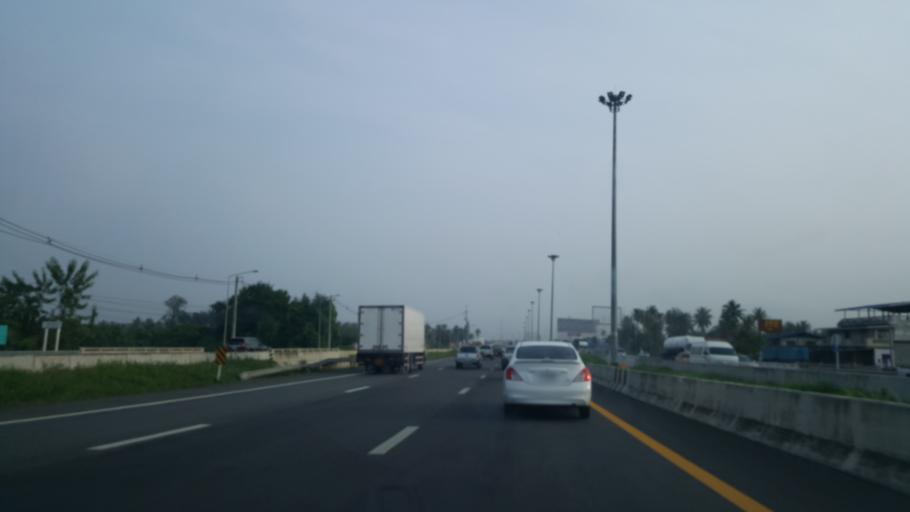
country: TH
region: Chon Buri
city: Ban Talat Bueng
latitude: 13.0031
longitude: 100.9933
